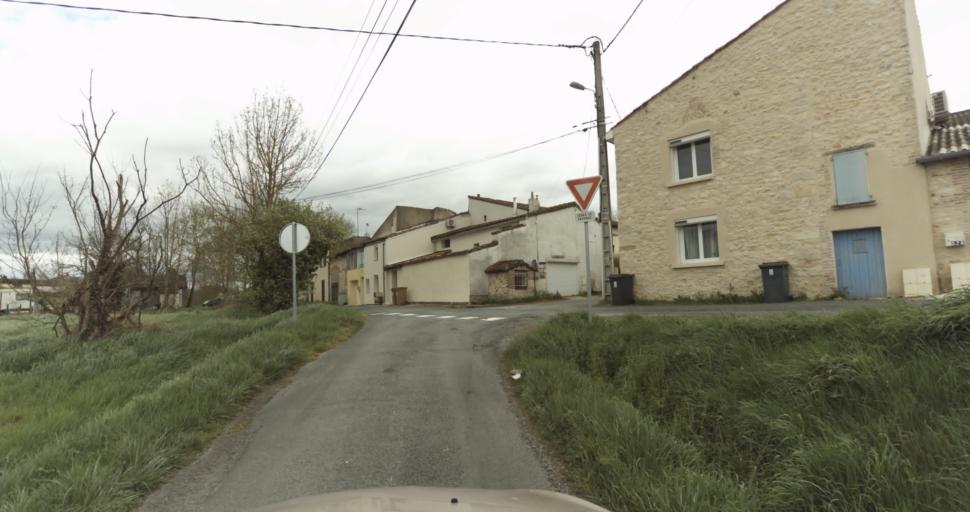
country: FR
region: Midi-Pyrenees
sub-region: Departement du Tarn
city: Puygouzon
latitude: 43.8953
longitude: 2.1607
